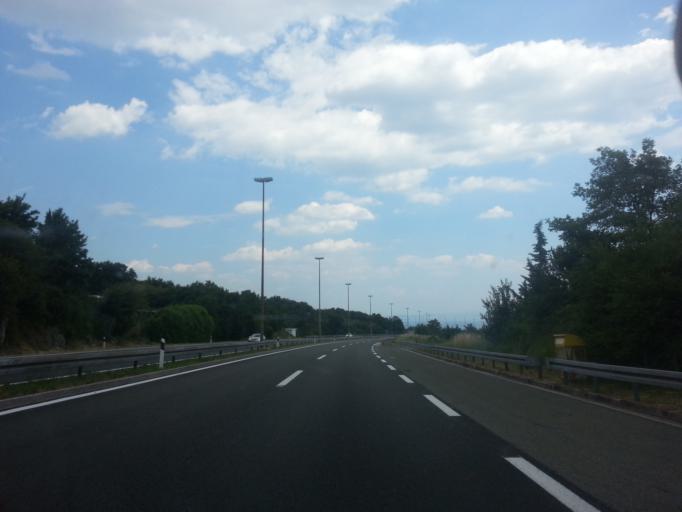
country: HR
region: Primorsko-Goranska
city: Matulji
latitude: 45.3644
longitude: 14.3327
